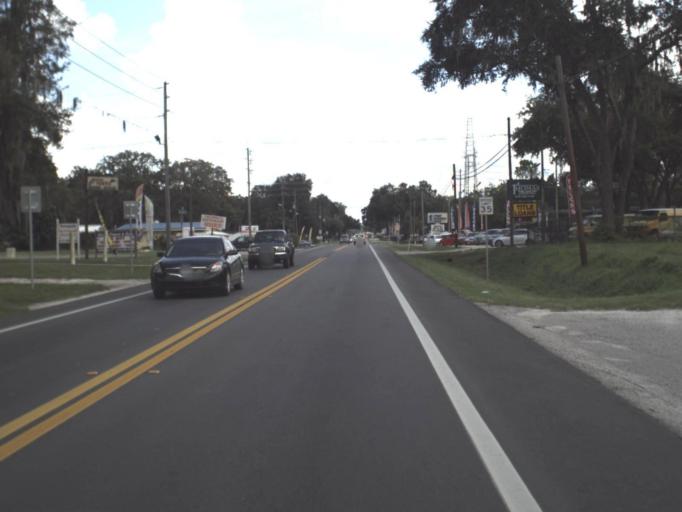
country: US
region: Florida
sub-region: Pasco County
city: Zephyrhills South
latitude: 28.2212
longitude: -82.1799
